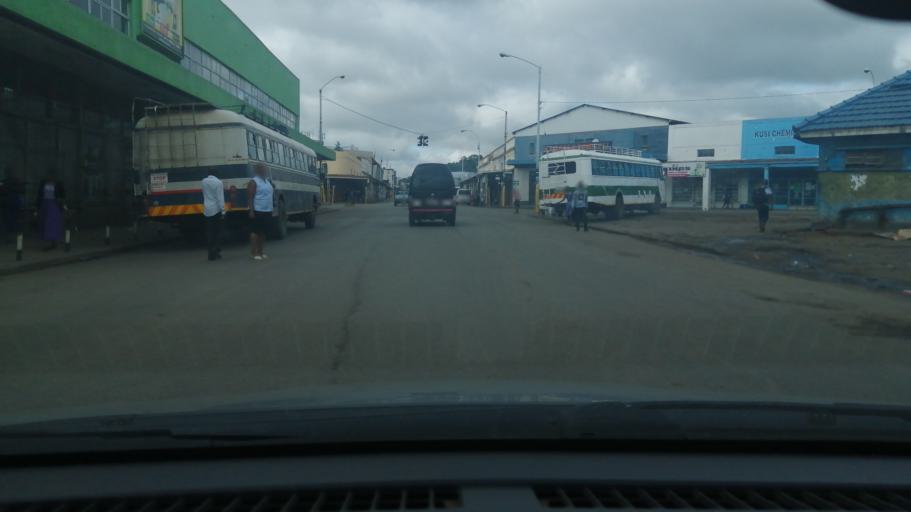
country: ZW
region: Harare
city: Harare
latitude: -17.8366
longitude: 31.0454
